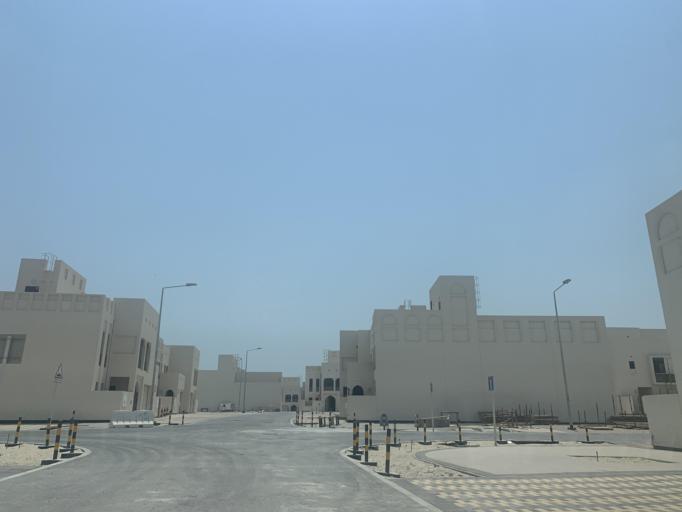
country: BH
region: Muharraq
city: Al Hadd
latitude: 26.2389
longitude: 50.6694
